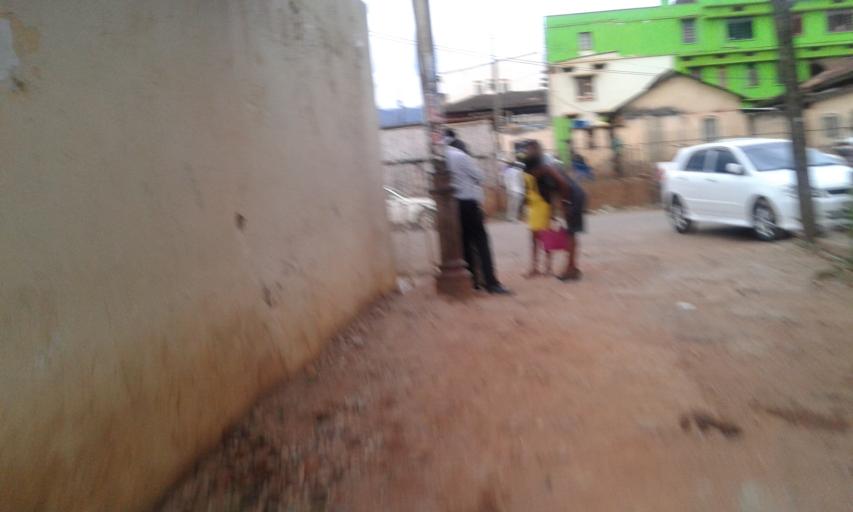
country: UG
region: Eastern Region
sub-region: Mbale District
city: Mbale
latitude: 1.0740
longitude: 34.1789
